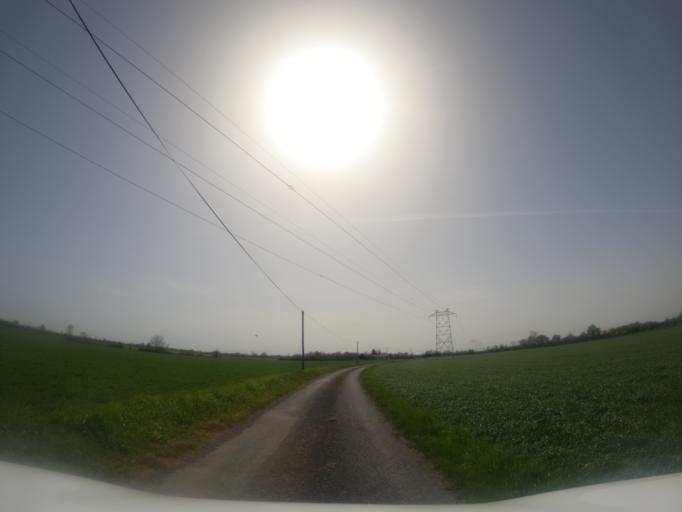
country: FR
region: Pays de la Loire
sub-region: Departement de la Vendee
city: Maillezais
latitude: 46.3858
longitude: -0.7964
